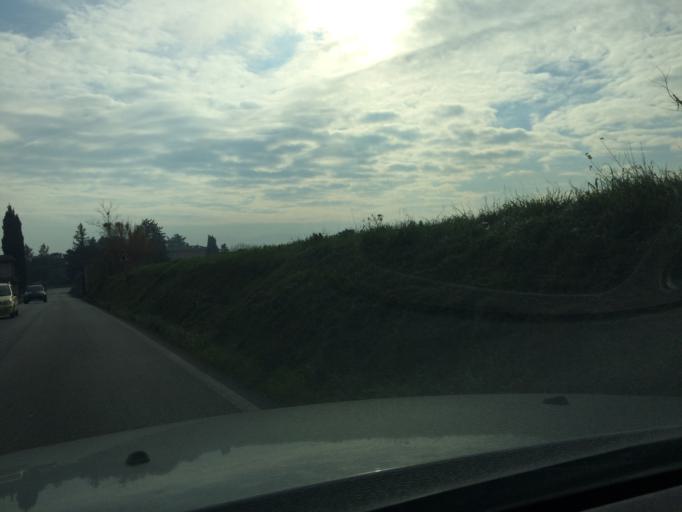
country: IT
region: Umbria
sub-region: Provincia di Perugia
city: Via Lippia
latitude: 43.0978
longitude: 12.4911
